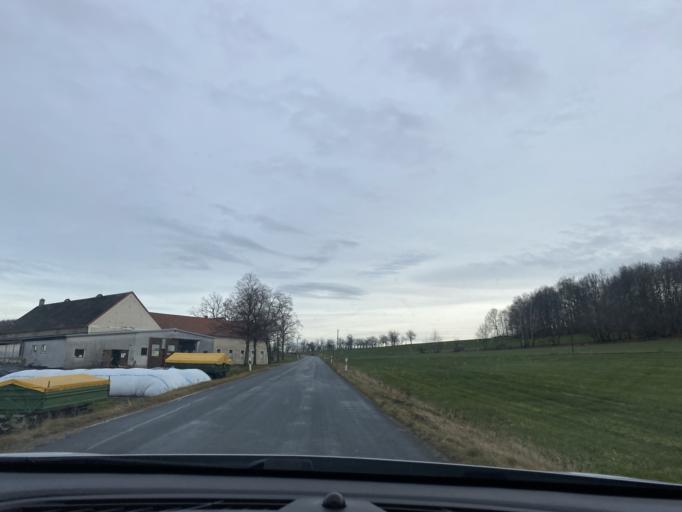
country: DE
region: Saxony
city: Schonau-Berzdorf
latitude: 51.0982
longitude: 14.8979
